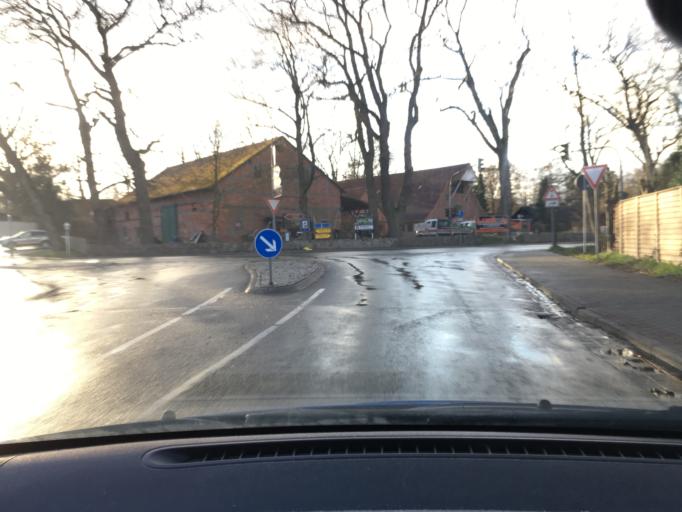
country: DE
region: Lower Saxony
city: Harmstorf
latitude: 53.3466
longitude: 9.9872
